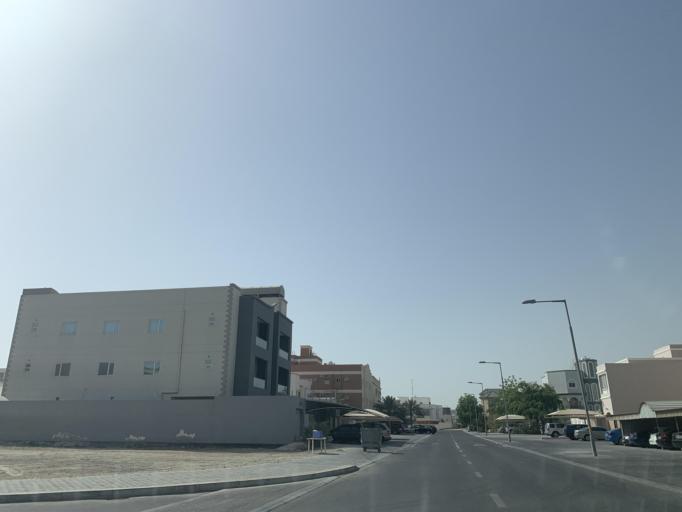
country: BH
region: Northern
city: Ar Rifa'
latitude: 26.1464
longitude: 50.5803
